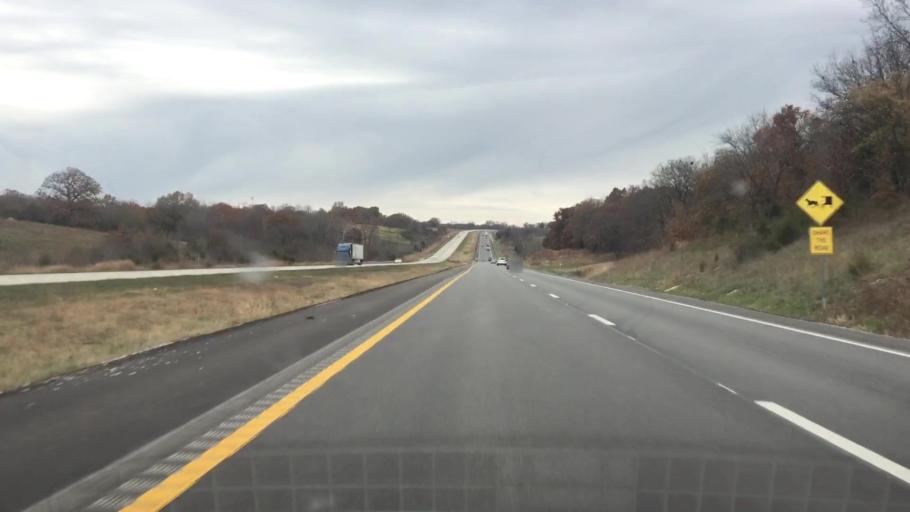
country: US
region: Missouri
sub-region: Saint Clair County
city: Osceola
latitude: 38.0150
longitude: -93.6617
